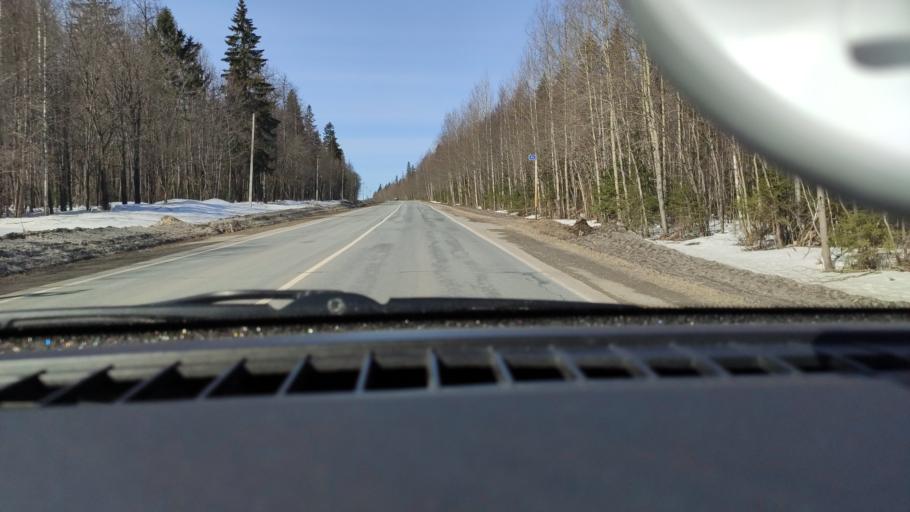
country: RU
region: Perm
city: Perm
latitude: 58.2076
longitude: 56.1946
